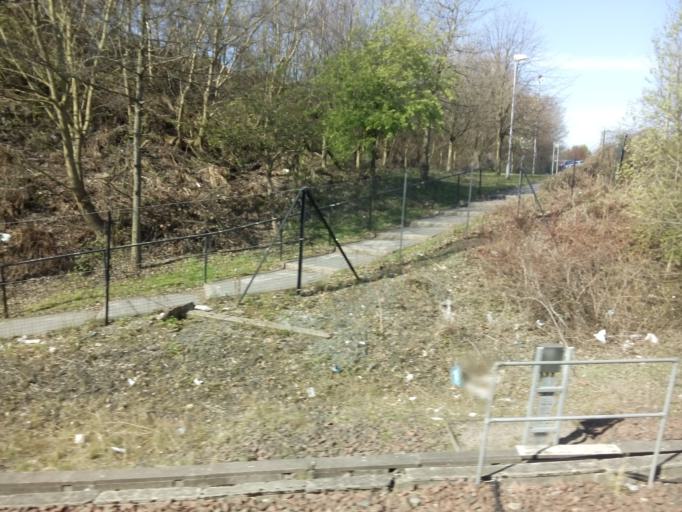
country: GB
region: Scotland
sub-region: Fife
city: Inverkeithing
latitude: 56.0370
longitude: -3.3957
